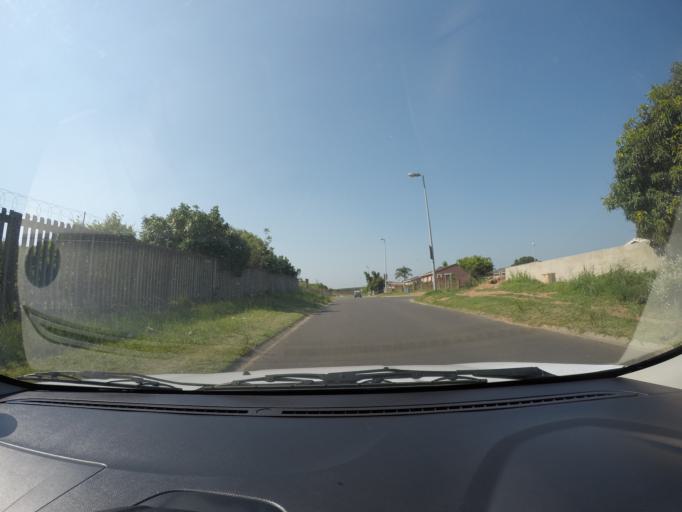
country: ZA
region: KwaZulu-Natal
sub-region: uThungulu District Municipality
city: Richards Bay
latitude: -28.7228
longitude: 32.0435
